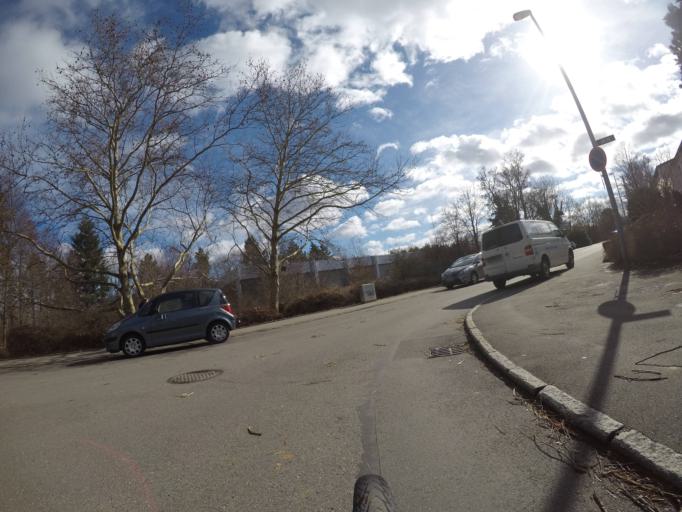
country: DE
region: Baden-Wuerttemberg
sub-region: Tuebingen Region
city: Sickenhausen
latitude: 48.5224
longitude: 9.2057
